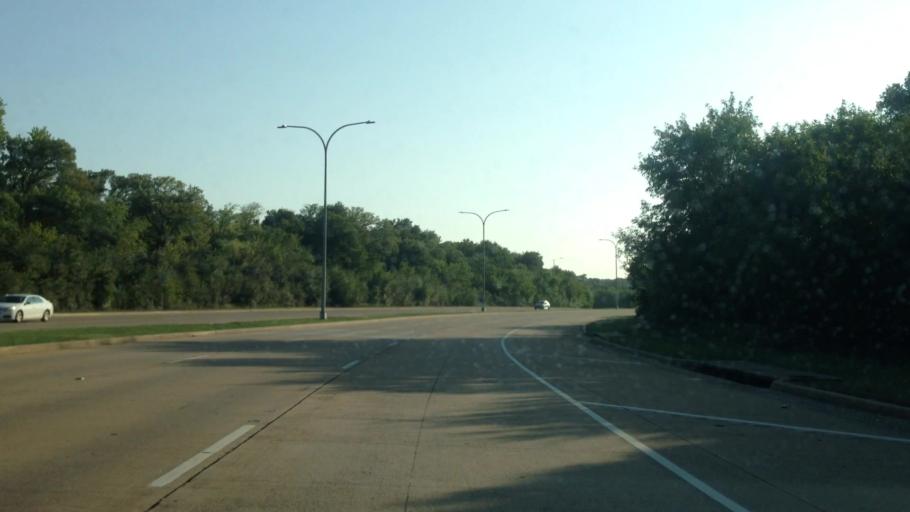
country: US
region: Texas
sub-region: Tarrant County
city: Pantego
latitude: 32.7380
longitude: -97.1764
